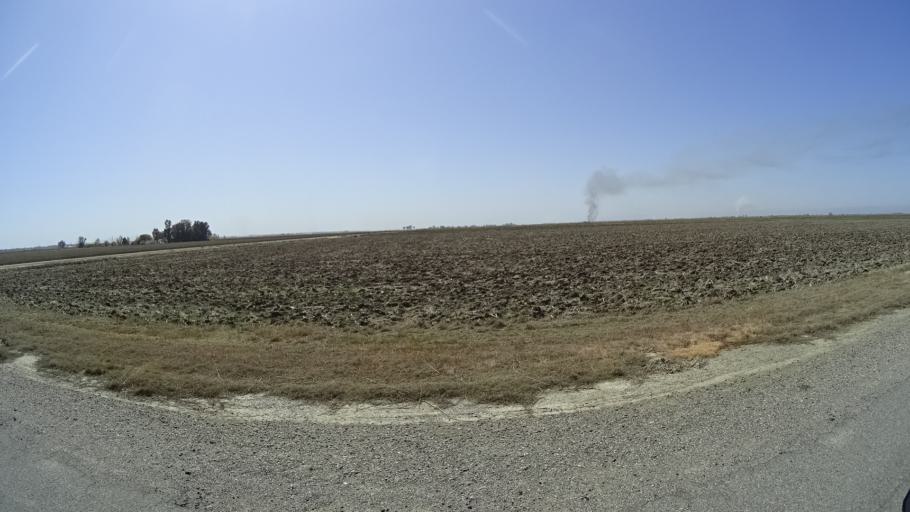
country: US
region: California
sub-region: Glenn County
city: Willows
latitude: 39.4286
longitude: -122.0563
